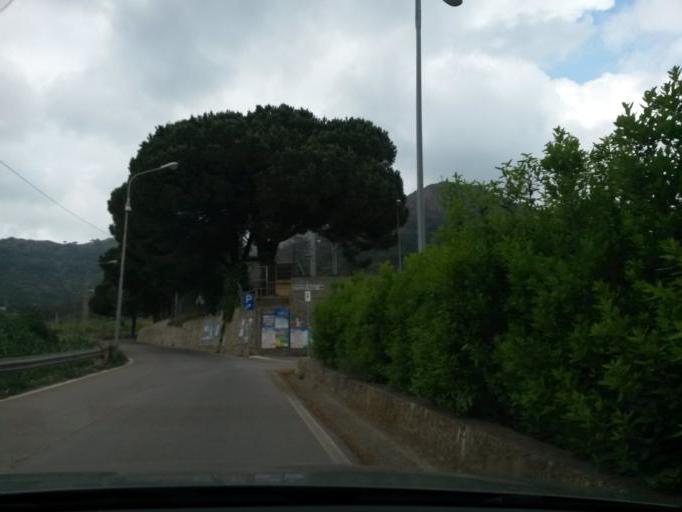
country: IT
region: Tuscany
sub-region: Provincia di Livorno
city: Porto Azzurro
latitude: 42.7701
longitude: 10.3904
